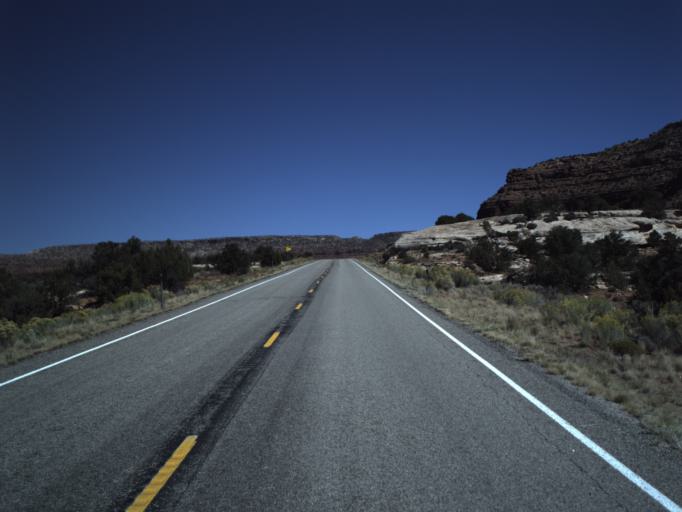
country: US
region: Utah
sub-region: San Juan County
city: Blanding
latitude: 37.6415
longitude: -110.1465
